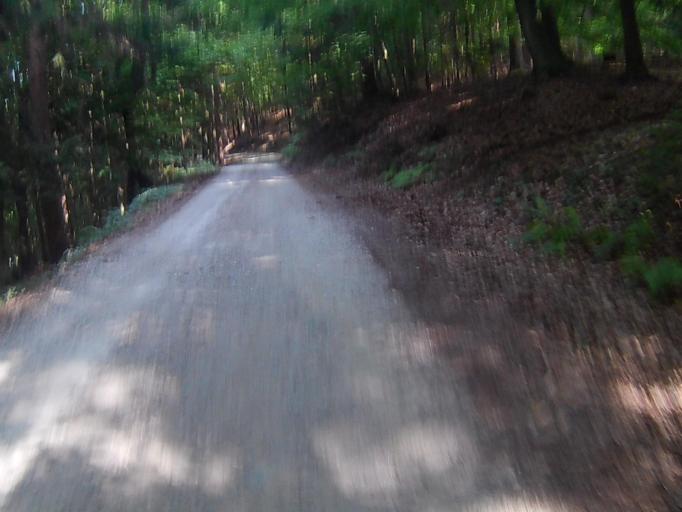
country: SI
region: Maribor
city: Pekre
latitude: 46.5229
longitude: 15.5803
